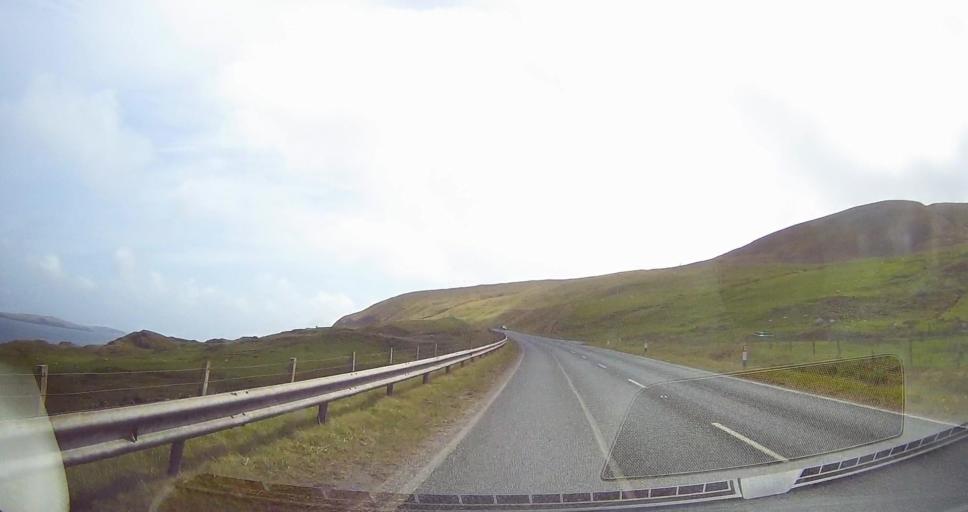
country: GB
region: Scotland
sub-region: Shetland Islands
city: Sandwick
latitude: 60.0273
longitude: -1.2365
